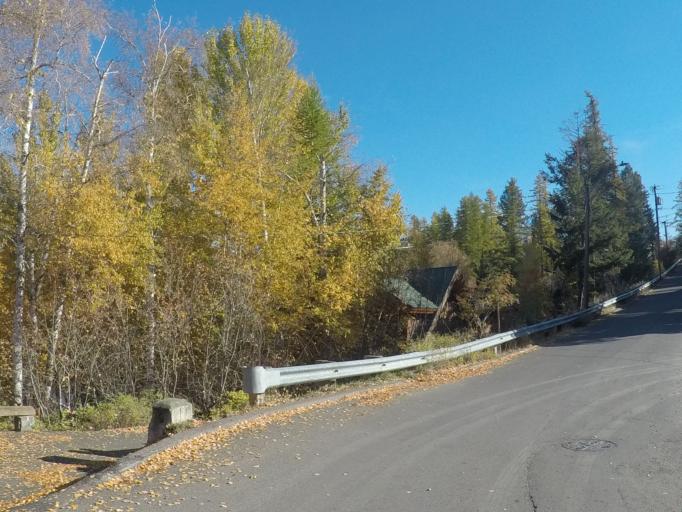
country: US
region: Montana
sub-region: Flathead County
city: Whitefish
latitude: 48.4180
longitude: -114.3496
